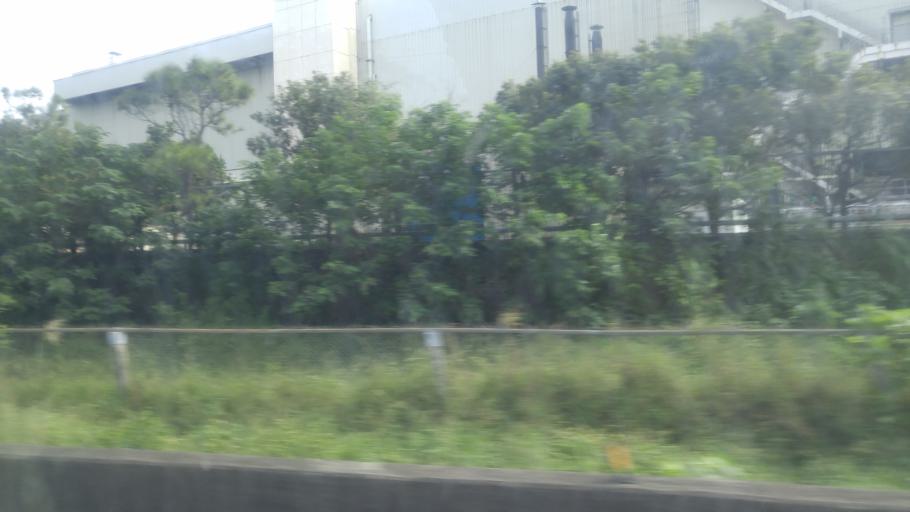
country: TW
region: Taiwan
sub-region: Hsinchu
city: Zhubei
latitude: 24.8951
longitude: 121.1320
